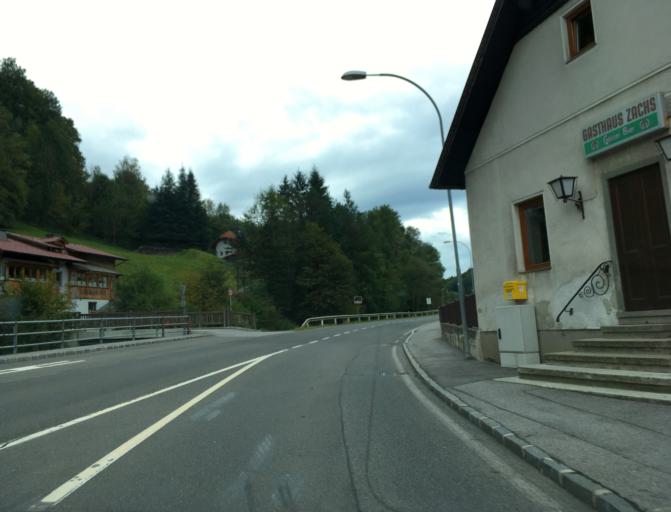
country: AT
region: Lower Austria
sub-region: Politischer Bezirk Neunkirchen
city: Thomasberg
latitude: 47.5681
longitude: 16.1427
